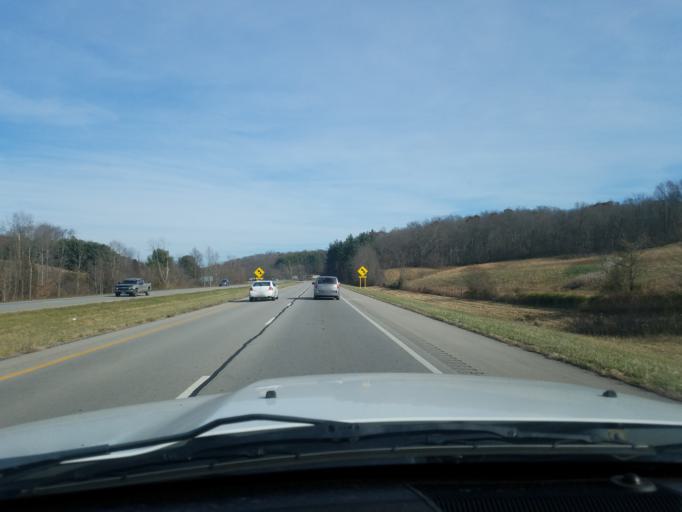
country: US
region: Ohio
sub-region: Jackson County
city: Jackson
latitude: 39.0521
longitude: -82.5961
